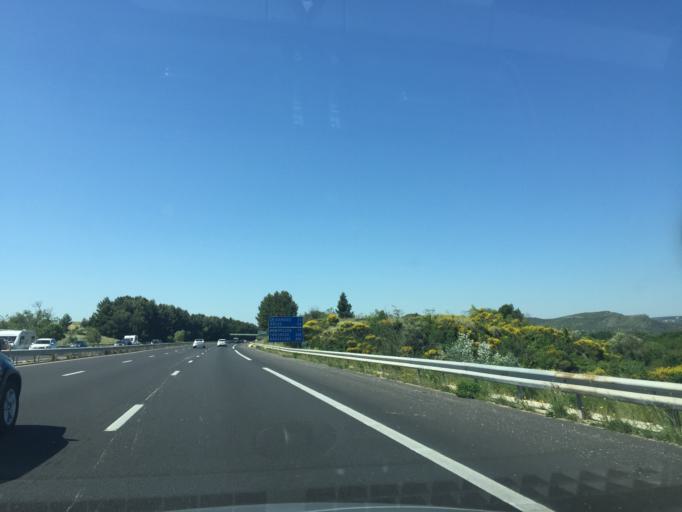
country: FR
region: Languedoc-Roussillon
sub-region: Departement du Gard
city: Remoulins
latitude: 43.9309
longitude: 4.5958
